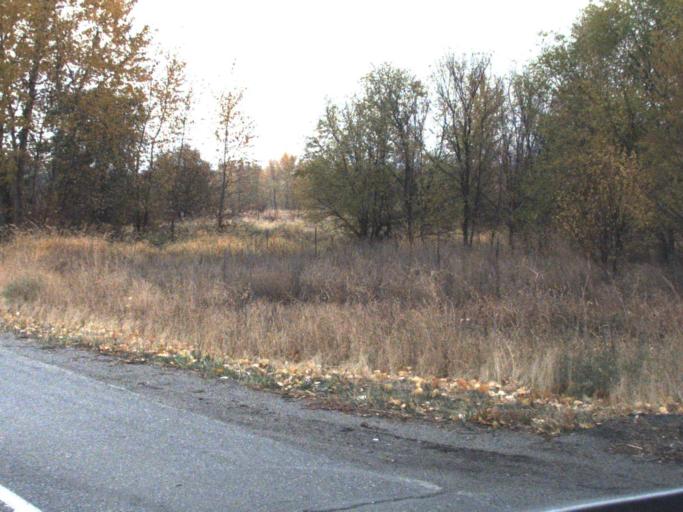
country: US
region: Washington
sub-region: Stevens County
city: Kettle Falls
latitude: 48.5958
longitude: -118.0030
